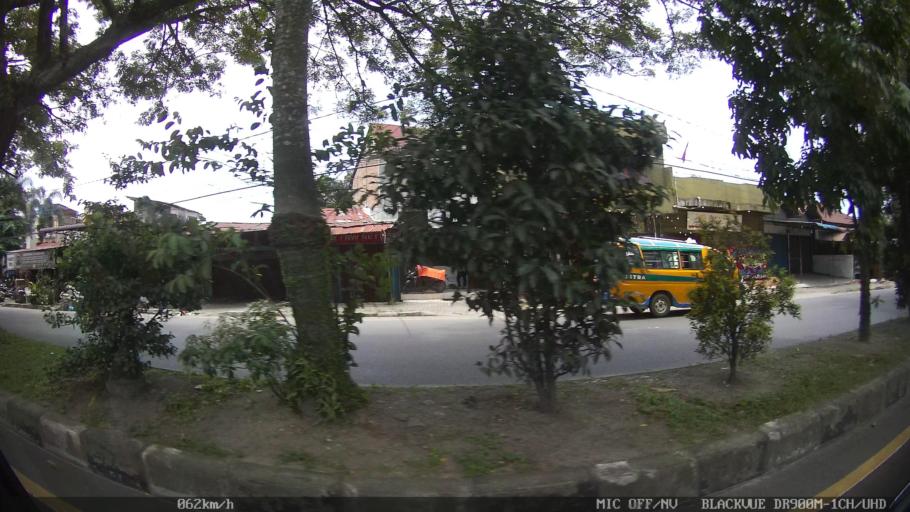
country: ID
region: North Sumatra
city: Sunggal
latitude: 3.5249
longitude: 98.6304
